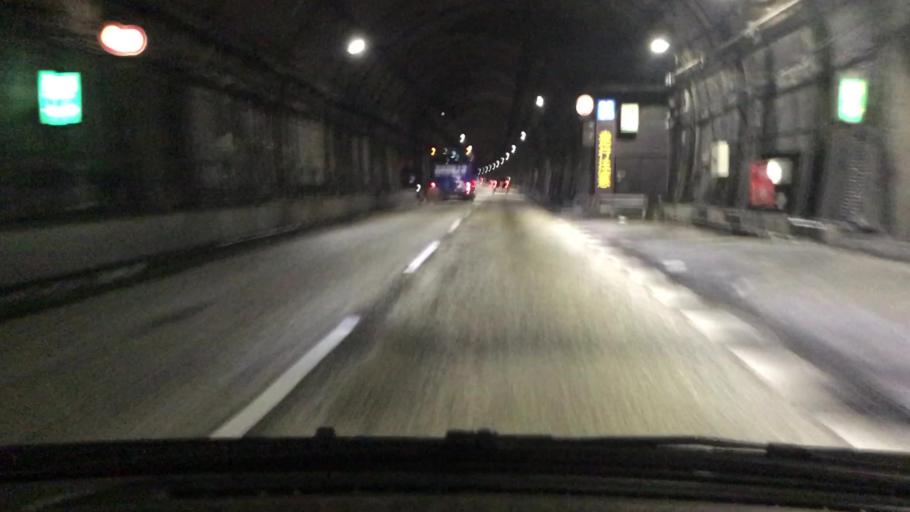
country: JP
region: Hyogo
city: Kobe
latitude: 34.7089
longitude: 135.1936
